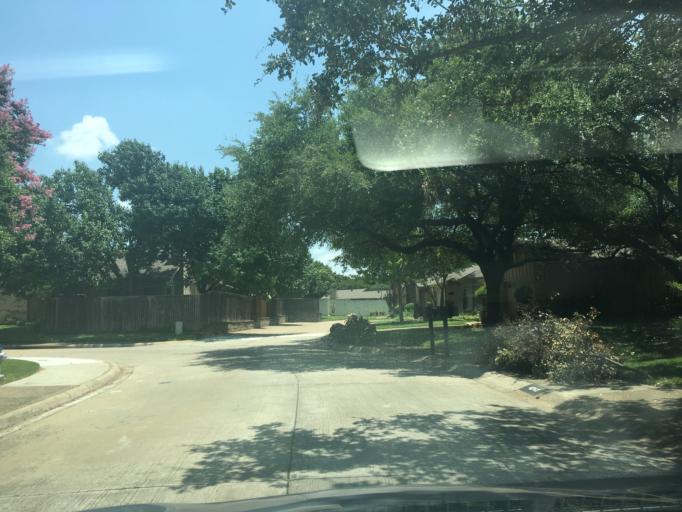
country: US
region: Texas
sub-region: Dallas County
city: Addison
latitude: 32.9203
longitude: -96.8453
